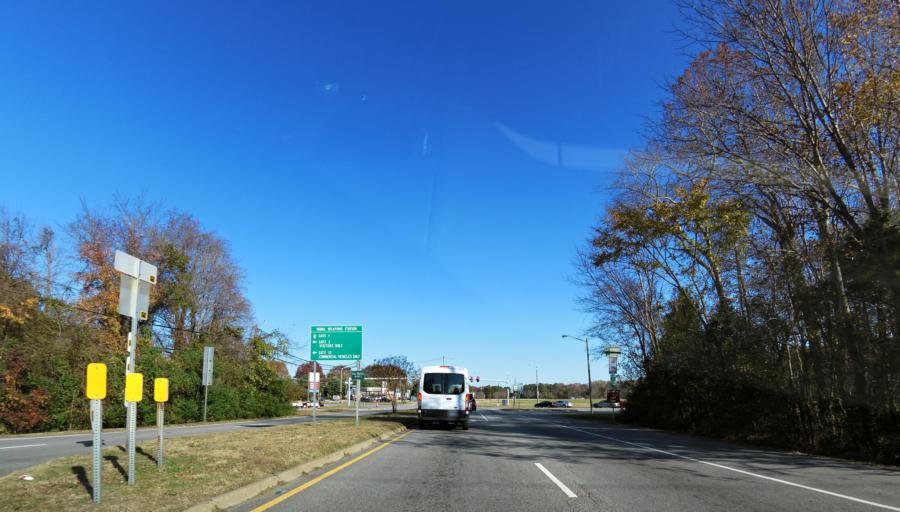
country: US
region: Virginia
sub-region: York County
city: Yorktown
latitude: 37.2060
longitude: -76.5741
